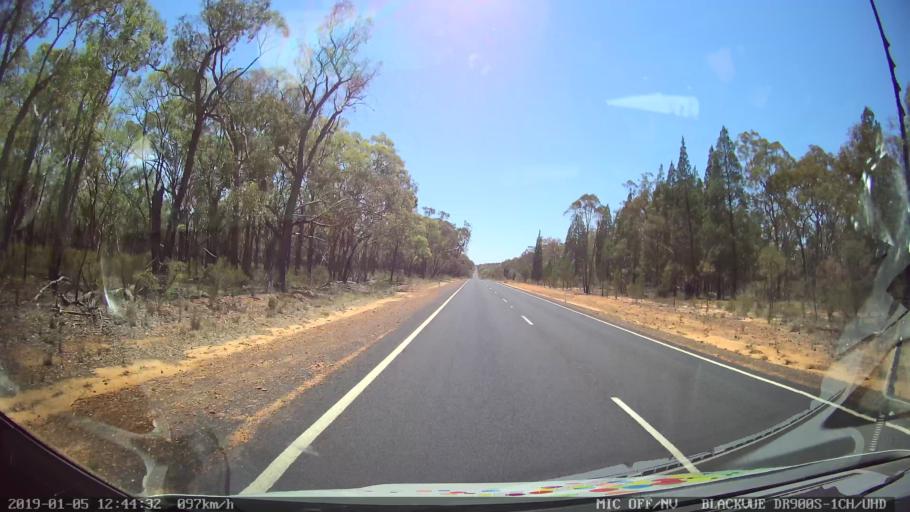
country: AU
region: New South Wales
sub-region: Warrumbungle Shire
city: Coonabarabran
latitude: -31.1368
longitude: 149.5384
